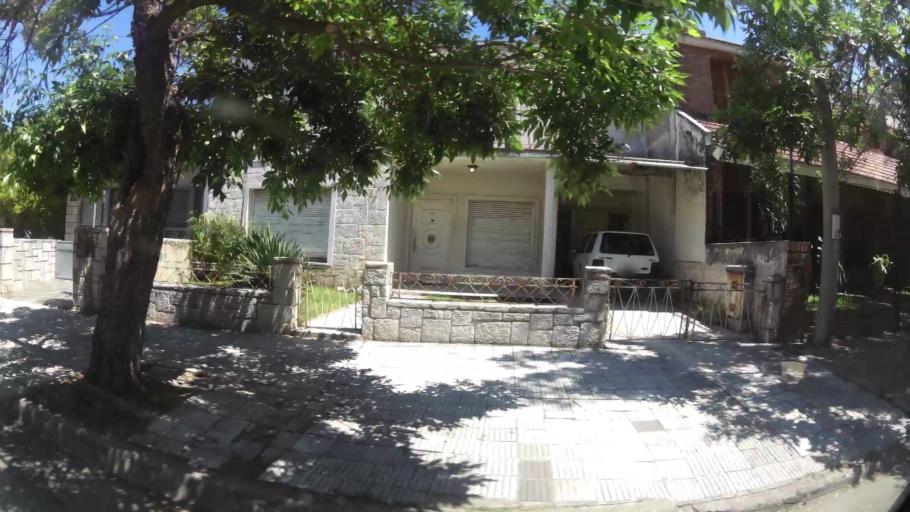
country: AR
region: Cordoba
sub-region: Departamento de Capital
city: Cordoba
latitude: -31.4109
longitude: -64.2024
